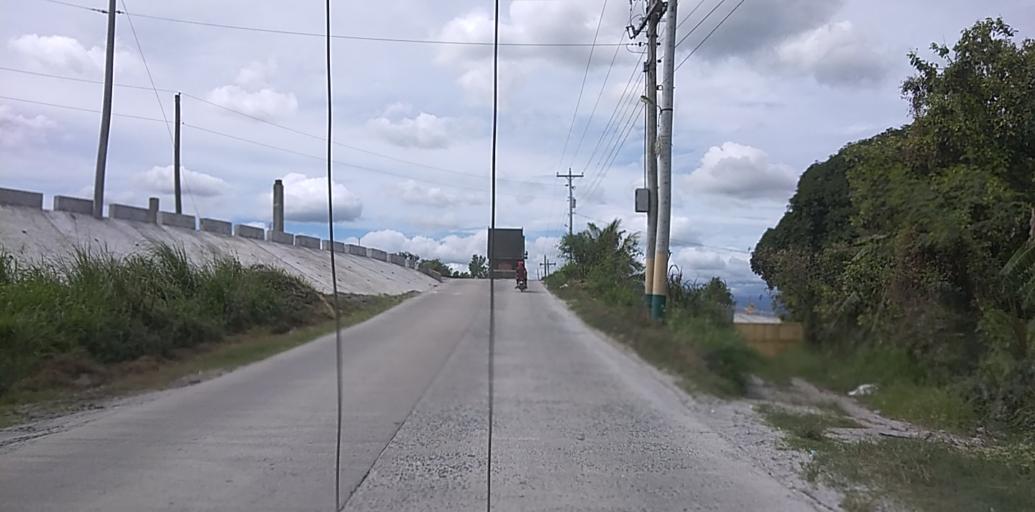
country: PH
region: Central Luzon
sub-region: Province of Pampanga
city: Porac
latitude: 15.0680
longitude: 120.5596
